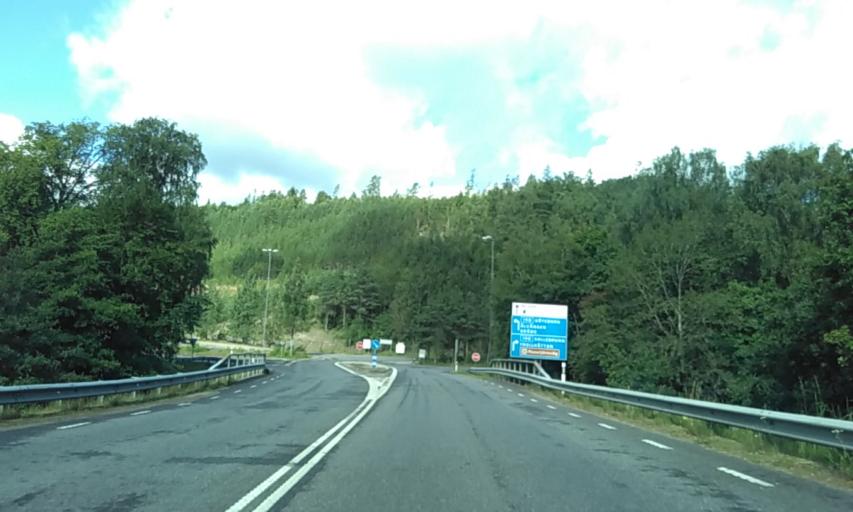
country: SE
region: Vaestra Goetaland
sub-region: Alingsas Kommun
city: Alingsas
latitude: 57.9755
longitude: 12.4350
